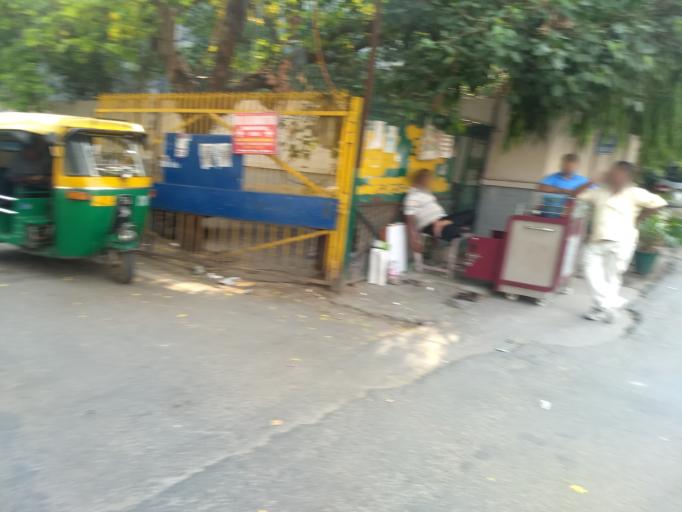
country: IN
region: NCT
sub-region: New Delhi
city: New Delhi
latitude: 28.5696
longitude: 77.2379
